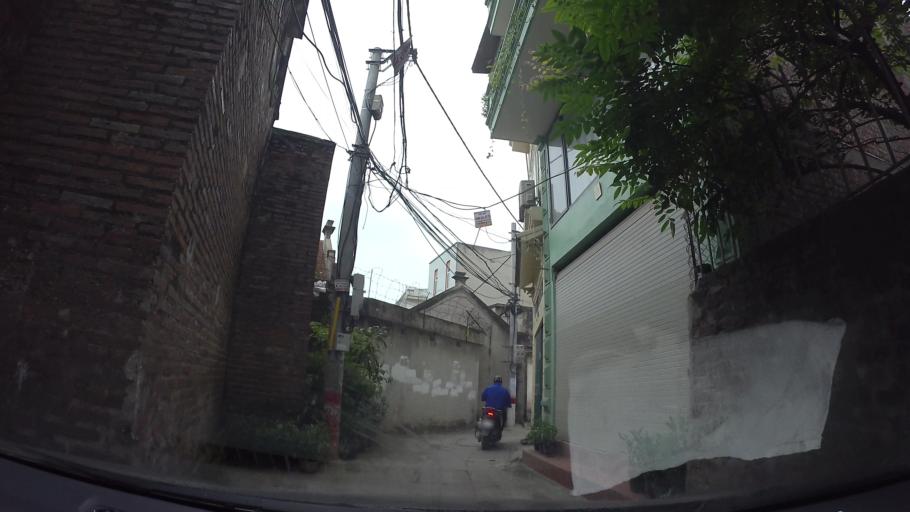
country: VN
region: Ha Noi
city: Van Dien
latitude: 20.9770
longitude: 105.8855
